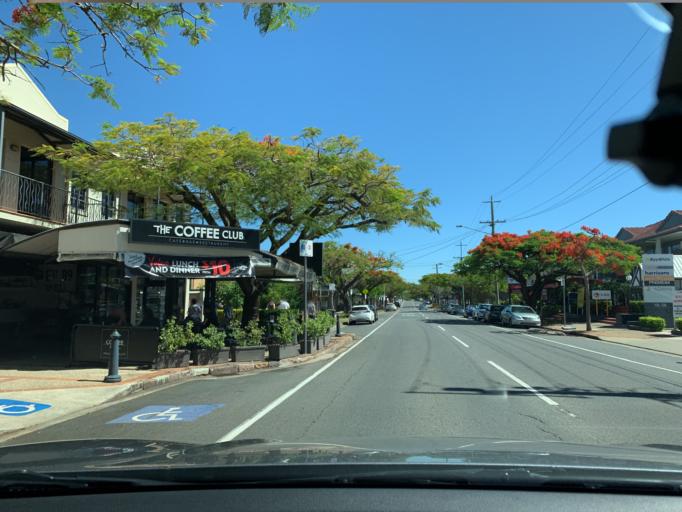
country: AU
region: Queensland
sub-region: Brisbane
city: Ascot
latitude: -27.4320
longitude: 153.0655
